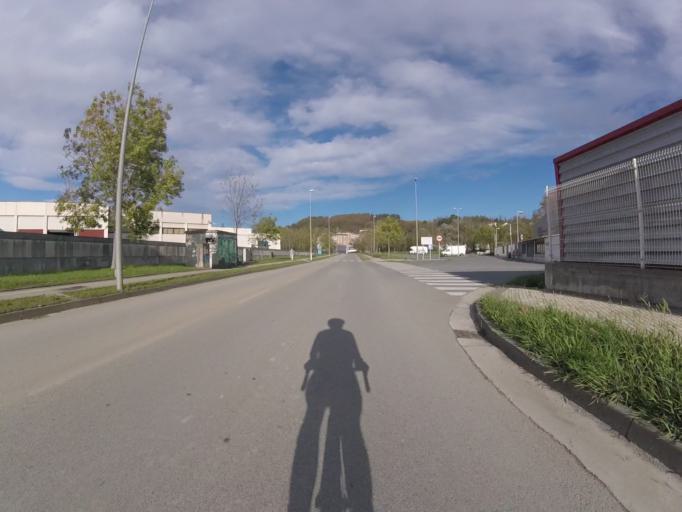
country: ES
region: Basque Country
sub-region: Provincia de Guipuzcoa
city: Hernani
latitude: 43.2687
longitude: -1.9622
